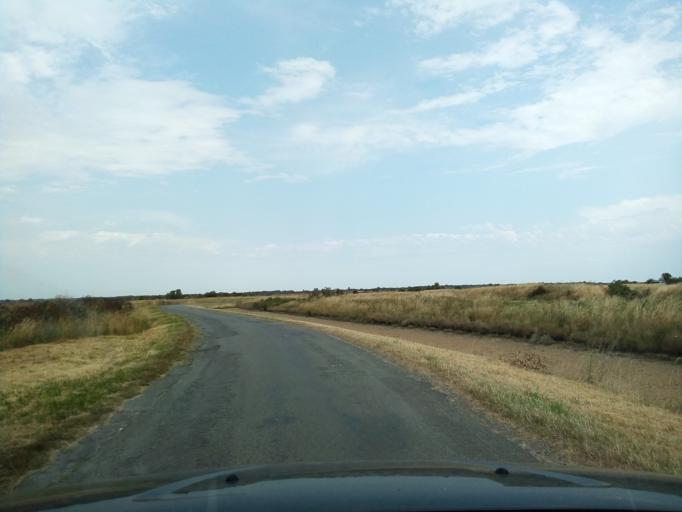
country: FR
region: Poitou-Charentes
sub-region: Departement de la Charente-Maritime
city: Dolus-d'Oleron
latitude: 45.9477
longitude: -1.2891
